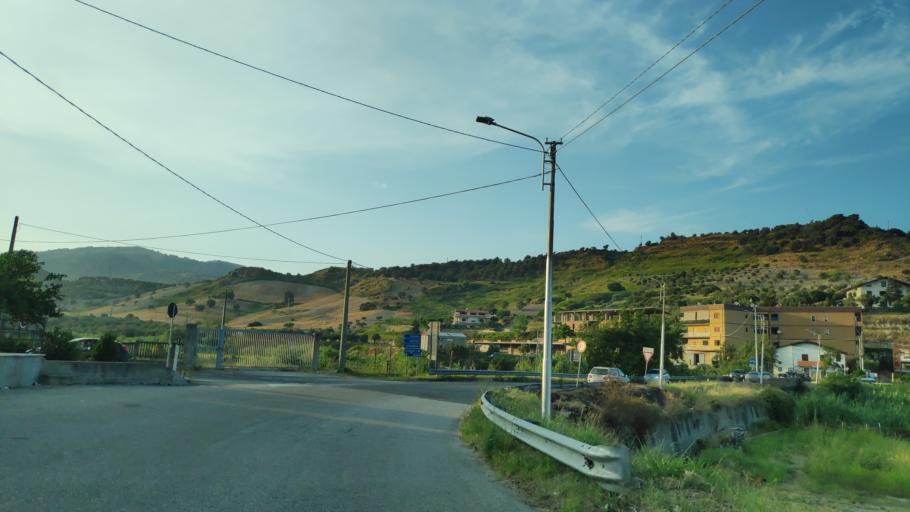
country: IT
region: Calabria
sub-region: Provincia di Catanzaro
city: Martelli-Laganosa
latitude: 38.6784
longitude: 16.5176
